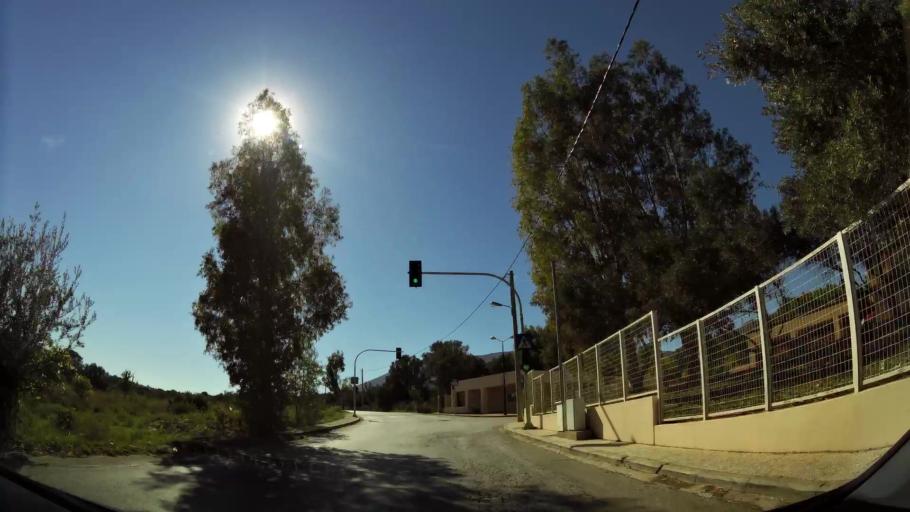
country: GR
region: Attica
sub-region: Nomarchia Anatolikis Attikis
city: Leondarion
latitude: 37.9781
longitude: 23.8654
